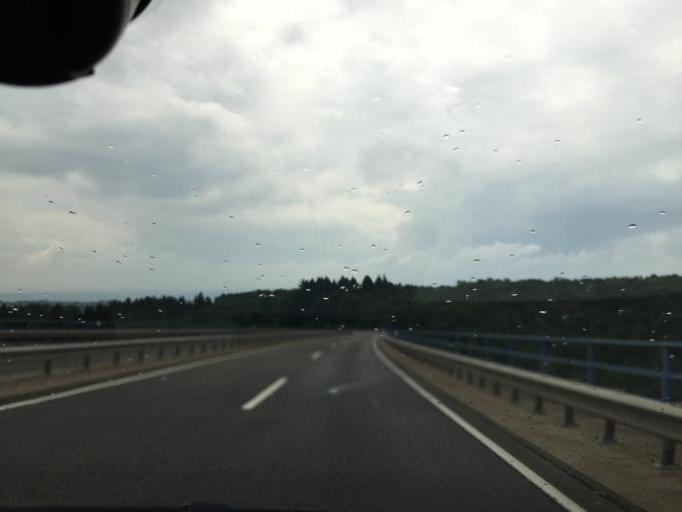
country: DE
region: Rheinland-Pfalz
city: Melsbach
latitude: 50.4867
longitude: 7.4960
